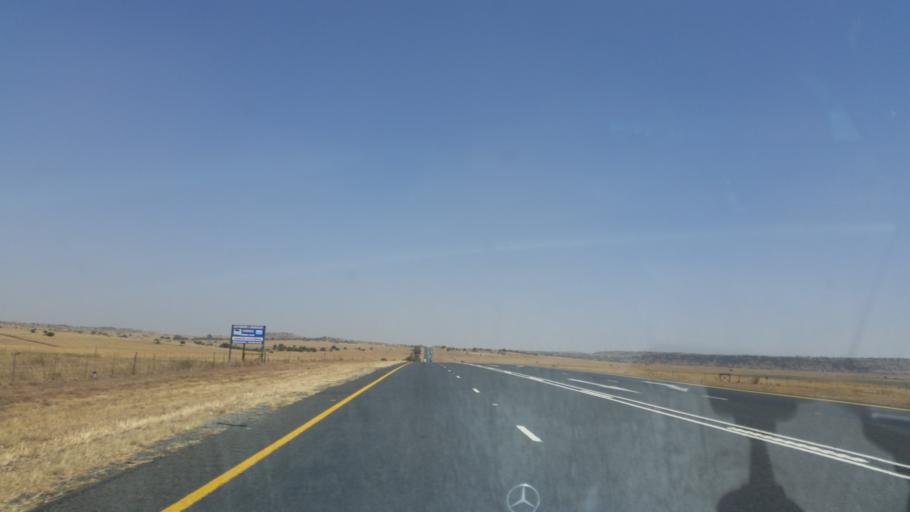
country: ZA
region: Orange Free State
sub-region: Lejweleputswa District Municipality
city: Winburg
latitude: -28.6819
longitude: 26.8280
